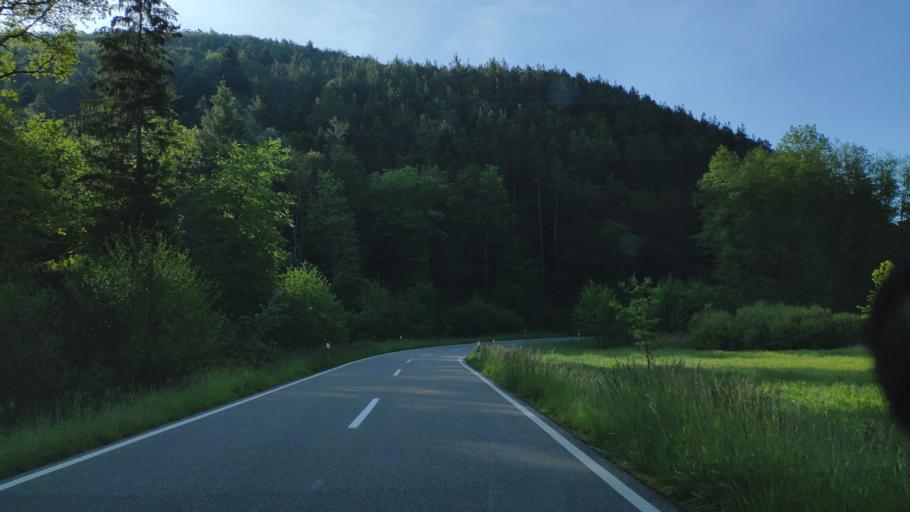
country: DE
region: Rheinland-Pfalz
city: Fischbach
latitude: 49.0834
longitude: 7.7351
